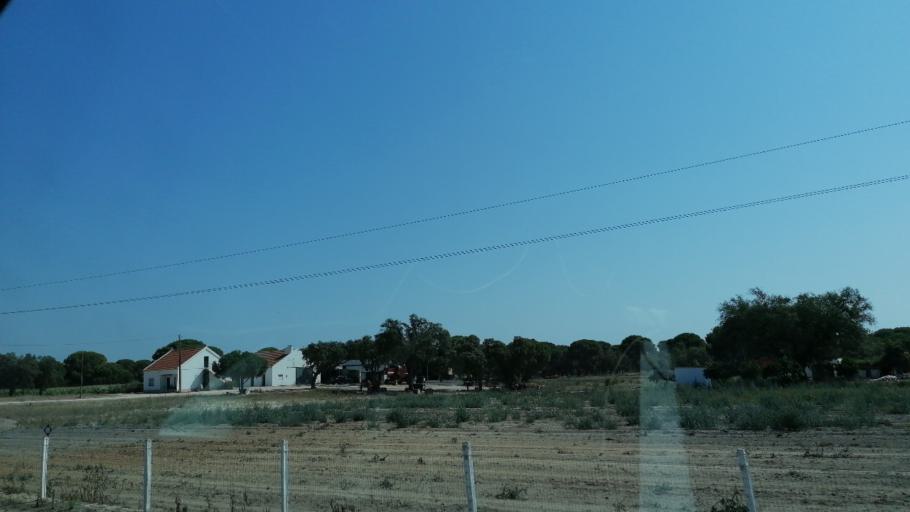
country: PT
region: Evora
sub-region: Vendas Novas
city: Vendas Novas
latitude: 38.7227
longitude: -8.6376
